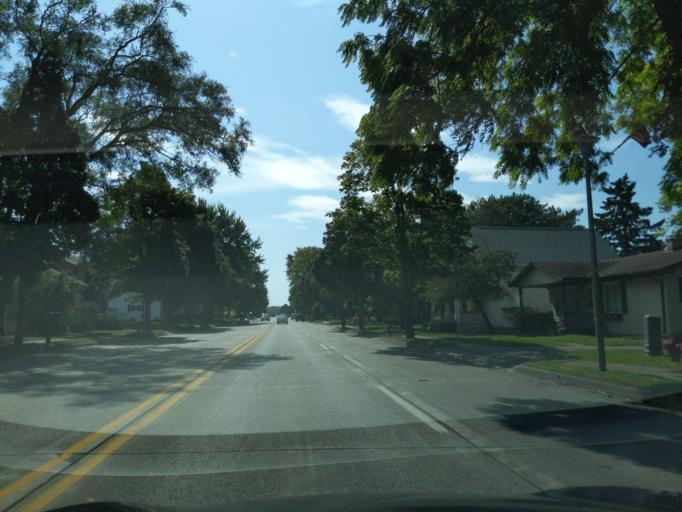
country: US
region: Michigan
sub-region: Saginaw County
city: Frankenmuth
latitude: 43.3203
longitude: -83.7405
